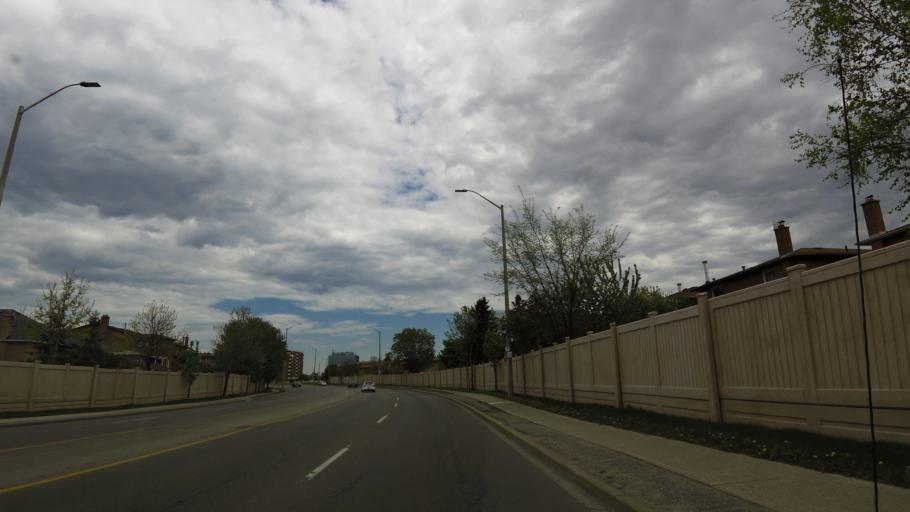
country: CA
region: Ontario
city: Mississauga
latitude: 43.5701
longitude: -79.6723
